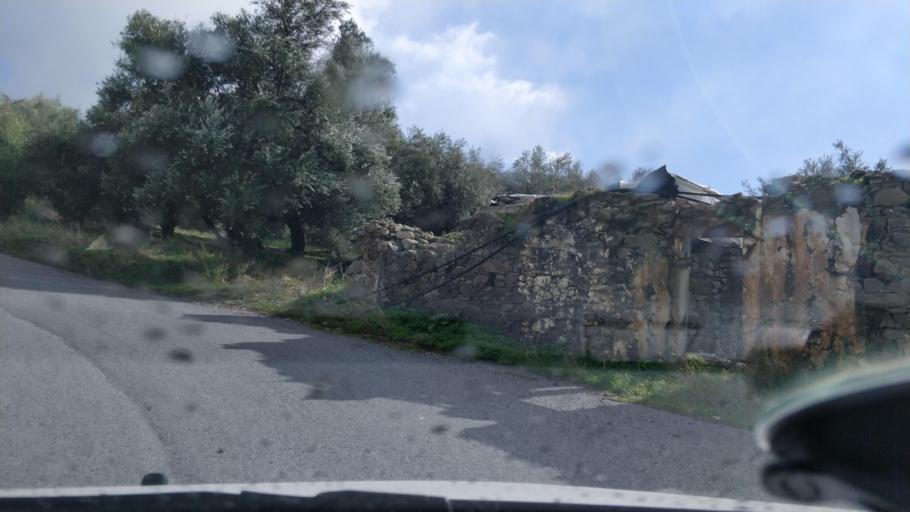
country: GR
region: Crete
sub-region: Nomos Lasithiou
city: Gra Liyia
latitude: 34.9955
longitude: 25.5087
